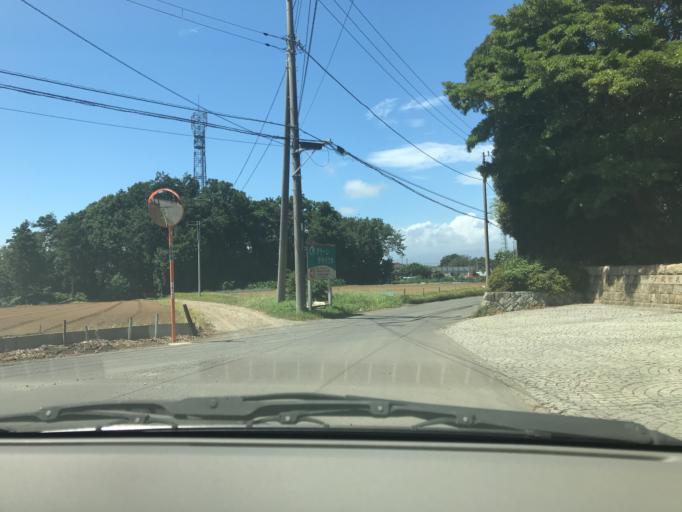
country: JP
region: Kanagawa
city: Fujisawa
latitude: 35.3525
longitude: 139.4400
